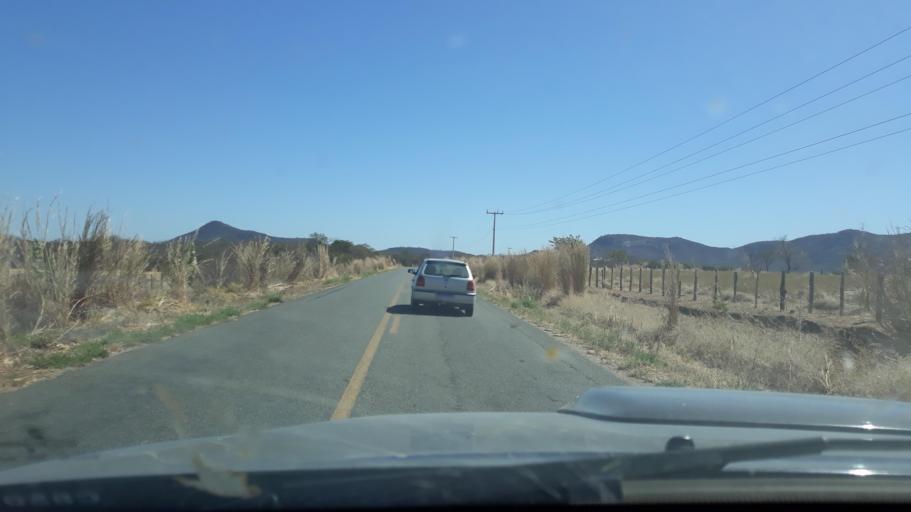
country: BR
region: Bahia
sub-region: Guanambi
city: Guanambi
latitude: -14.1669
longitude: -42.8132
